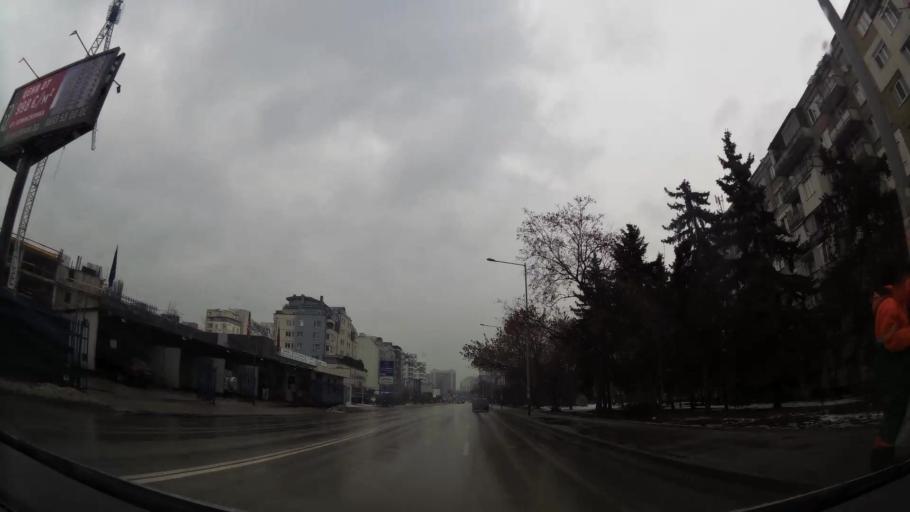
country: BG
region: Sofia-Capital
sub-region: Stolichna Obshtina
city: Sofia
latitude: 42.6663
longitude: 23.2851
